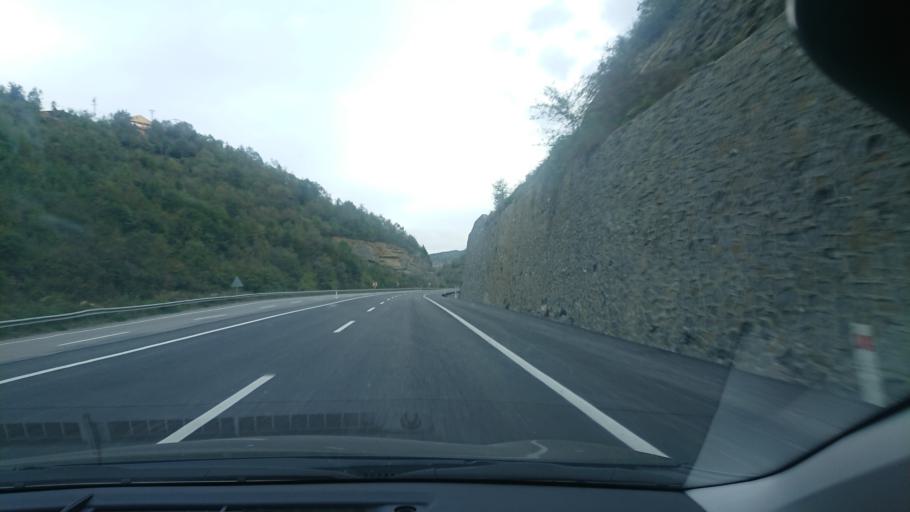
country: TR
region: Zonguldak
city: Beycuma
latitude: 41.3908
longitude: 31.9360
